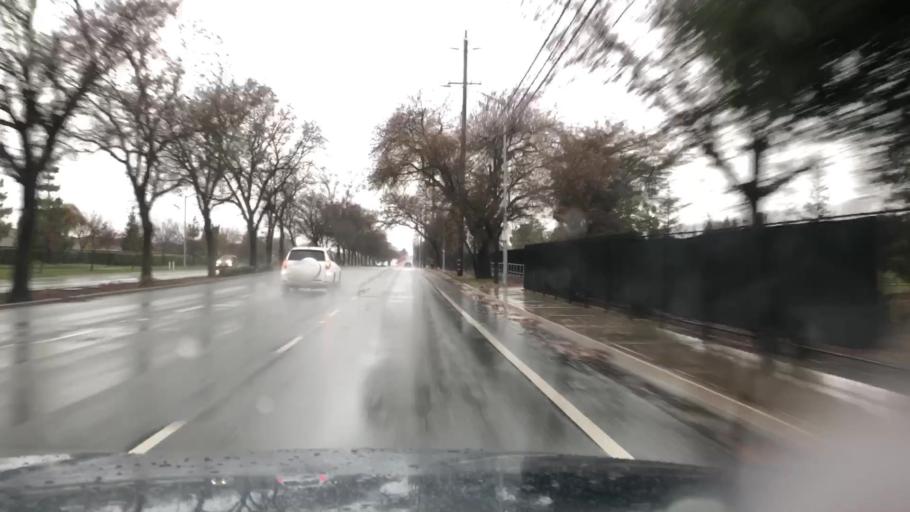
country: US
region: California
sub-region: Sacramento County
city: Laguna
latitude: 38.4088
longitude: -121.4420
